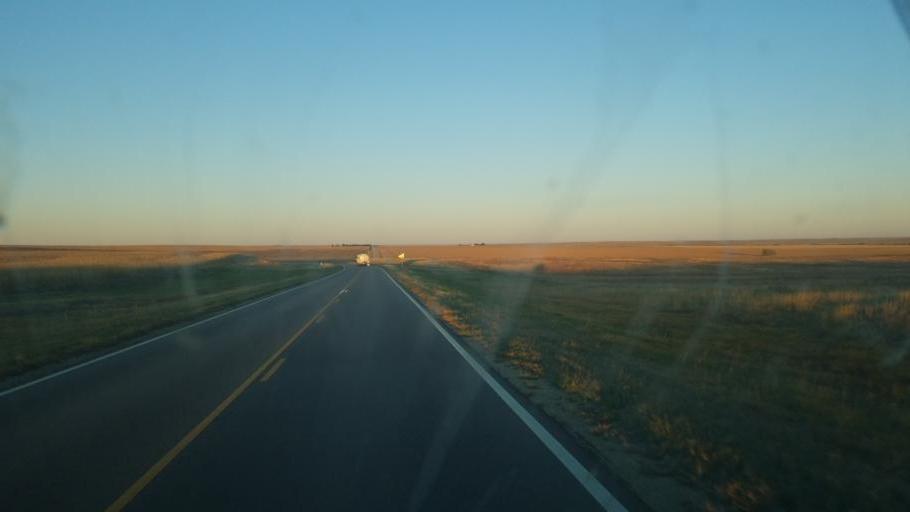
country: US
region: Kansas
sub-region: Wallace County
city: Sharon Springs
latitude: 38.9012
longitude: -101.8540
